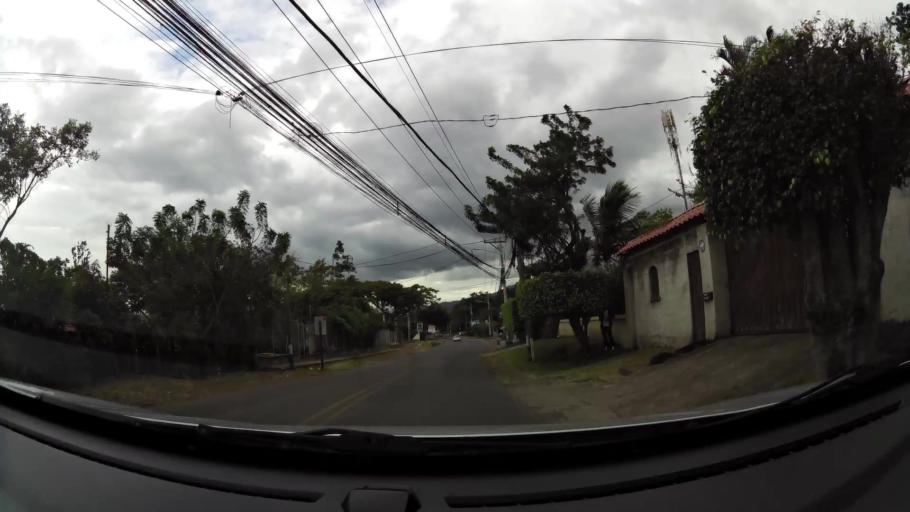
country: CR
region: Heredia
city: La Asuncion
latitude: 9.9546
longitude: -84.1673
